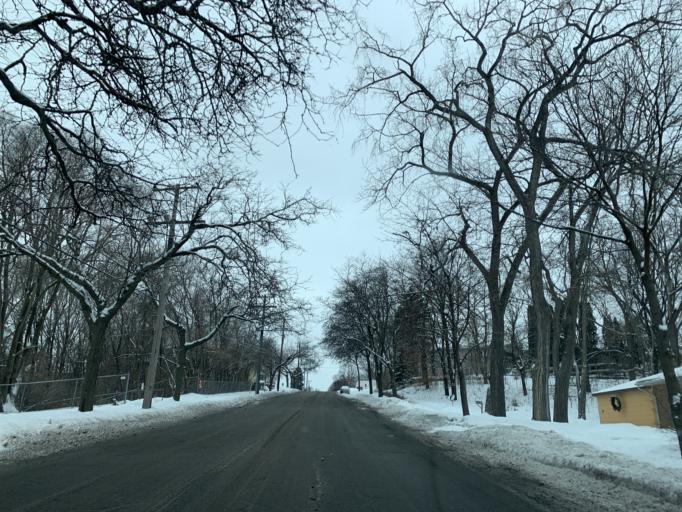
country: US
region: Minnesota
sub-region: Ramsey County
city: Saint Paul
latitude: 44.9846
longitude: -93.1141
